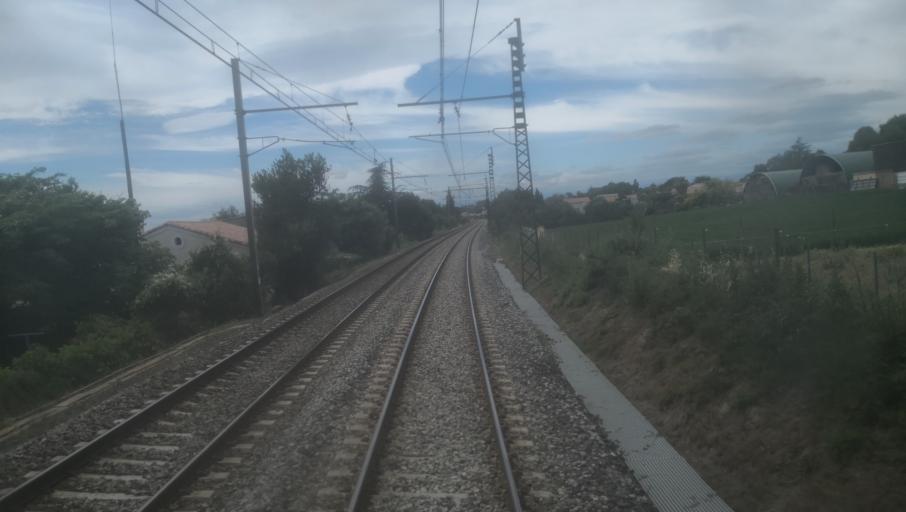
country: FR
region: Languedoc-Roussillon
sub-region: Departement de l'Herault
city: Cers
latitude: 43.3229
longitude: 3.3106
